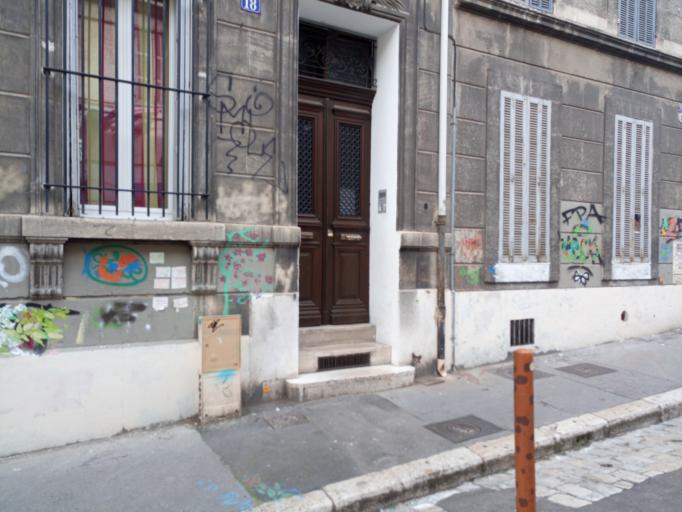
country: FR
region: Provence-Alpes-Cote d'Azur
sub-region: Departement des Bouches-du-Rhone
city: Marseille 01
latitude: 43.2900
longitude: 5.3882
